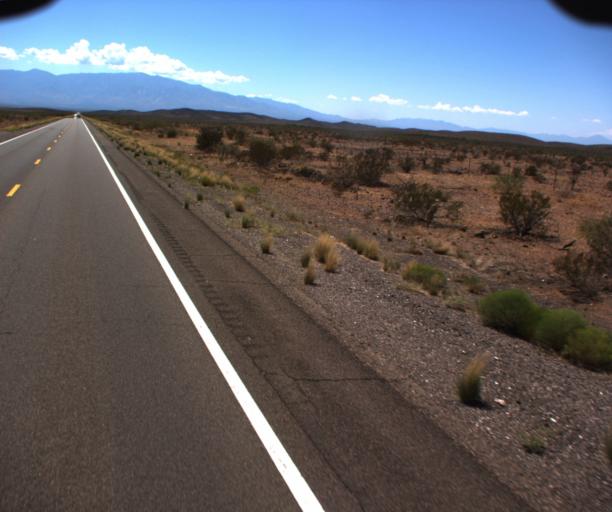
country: US
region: Arizona
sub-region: Graham County
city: Safford
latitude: 32.8188
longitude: -109.4810
